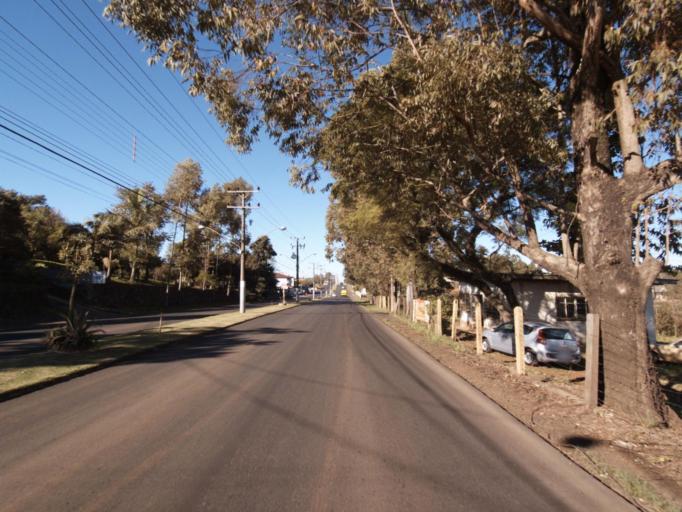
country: AR
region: Misiones
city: Bernardo de Irigoyen
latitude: -26.7493
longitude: -53.5009
